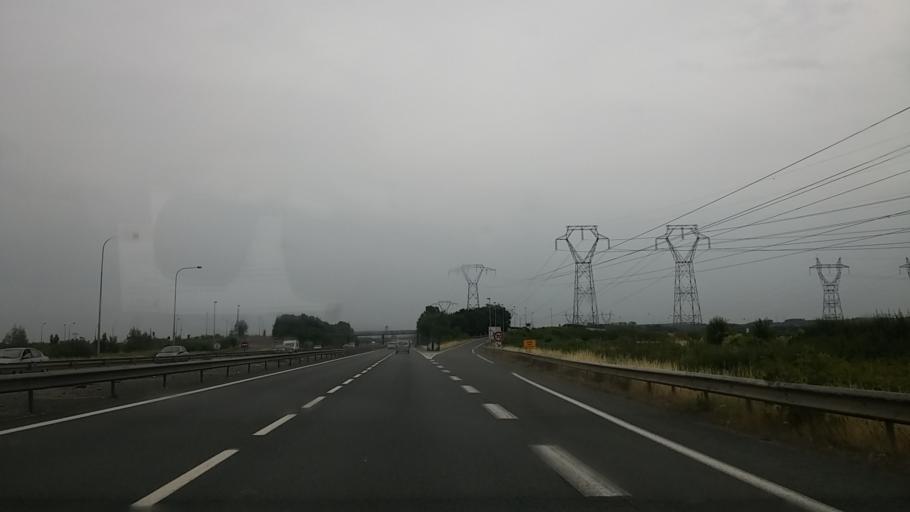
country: FR
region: Ile-de-France
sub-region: Departement de Seine-et-Marne
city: Mitry-Mory
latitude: 48.9678
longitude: 2.6026
